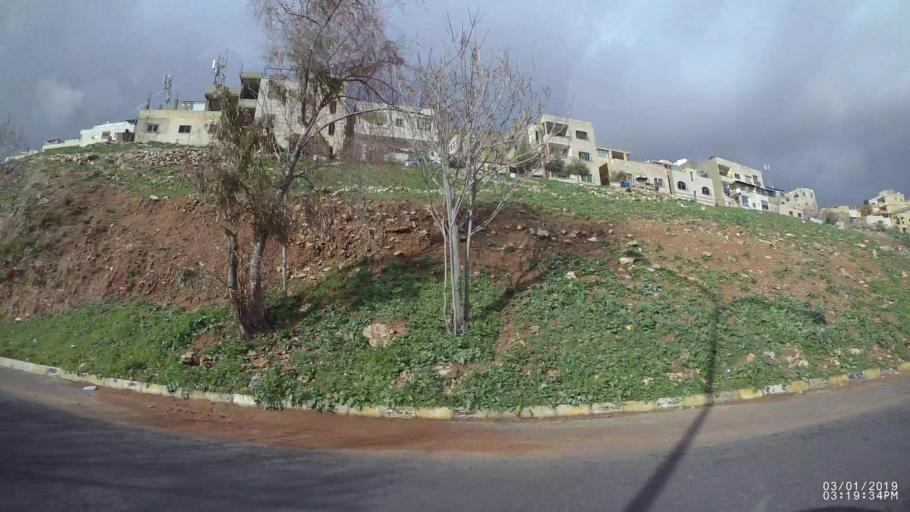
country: JO
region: Amman
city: Amman
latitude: 31.9405
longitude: 35.9009
